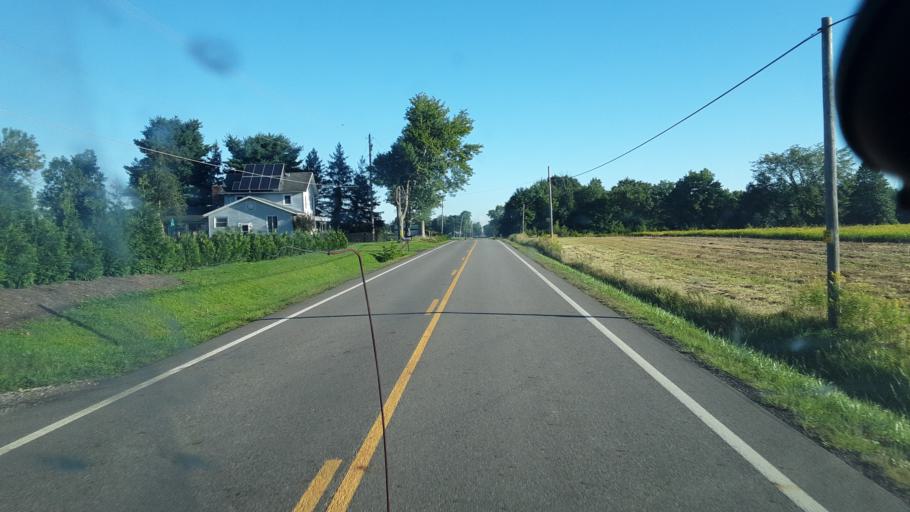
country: US
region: Ohio
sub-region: Trumbull County
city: Champion Heights
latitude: 41.3787
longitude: -80.9547
